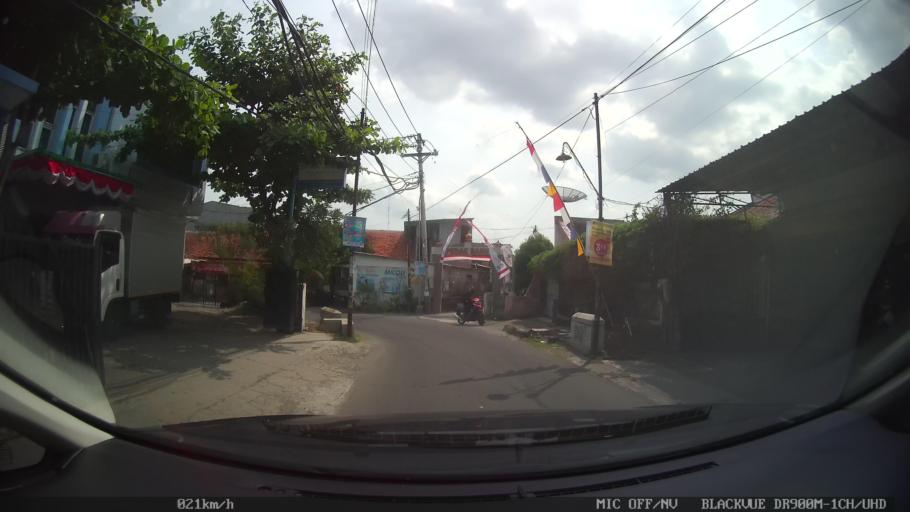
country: ID
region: Daerah Istimewa Yogyakarta
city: Yogyakarta
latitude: -7.7876
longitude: 110.3988
